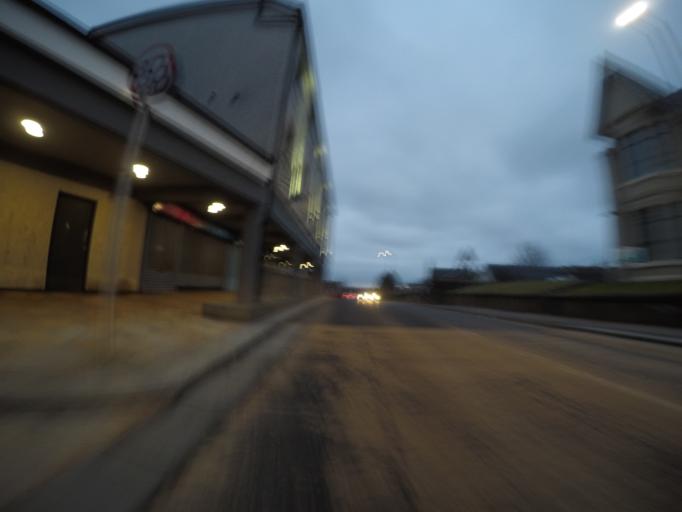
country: GB
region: Scotland
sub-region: North Ayrshire
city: Kilwinning
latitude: 55.6534
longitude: -4.7013
